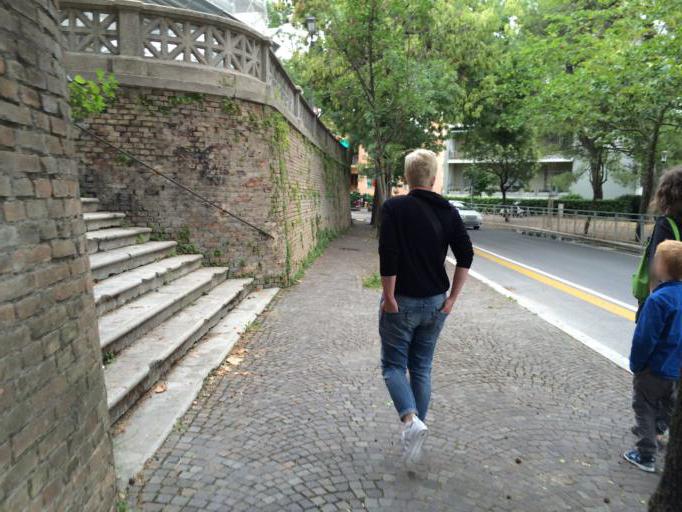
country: IT
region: The Marches
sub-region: Provincia di Pesaro e Urbino
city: Pesaro
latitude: 43.9103
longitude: 12.9158
